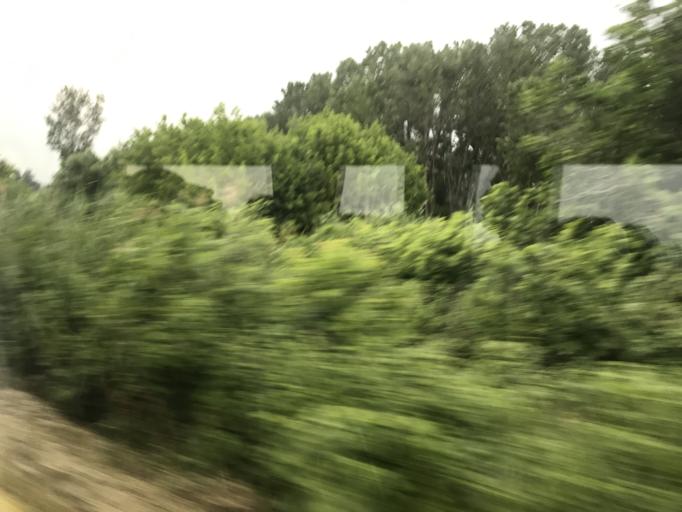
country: GR
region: East Macedonia and Thrace
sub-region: Nomos Rodopis
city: Aratos
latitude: 41.0791
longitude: 25.5673
